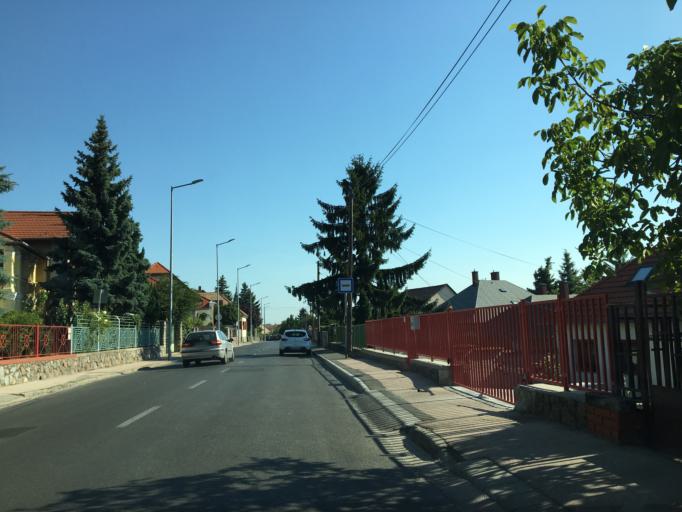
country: HU
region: Tolna
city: Szekszard
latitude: 46.3453
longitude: 18.6976
